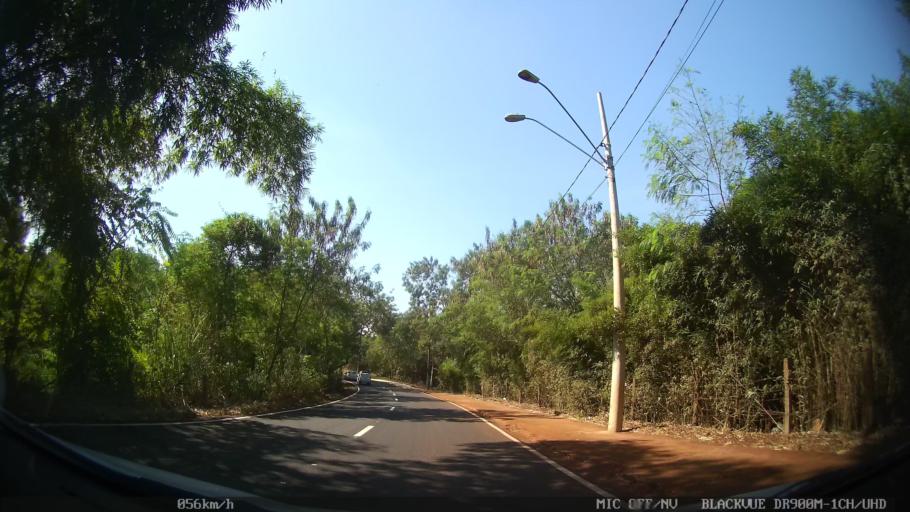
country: BR
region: Sao Paulo
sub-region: Ribeirao Preto
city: Ribeirao Preto
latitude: -21.2058
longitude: -47.8283
